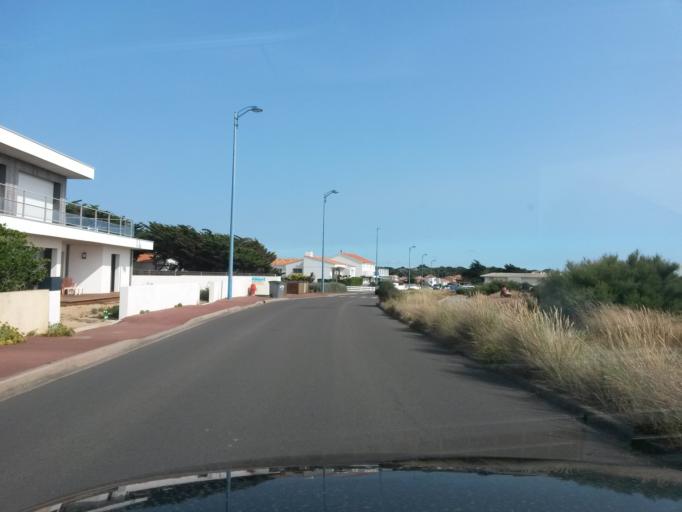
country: FR
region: Pays de la Loire
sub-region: Departement de la Vendee
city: Bretignolles-sur-Mer
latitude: 46.6300
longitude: -1.8781
